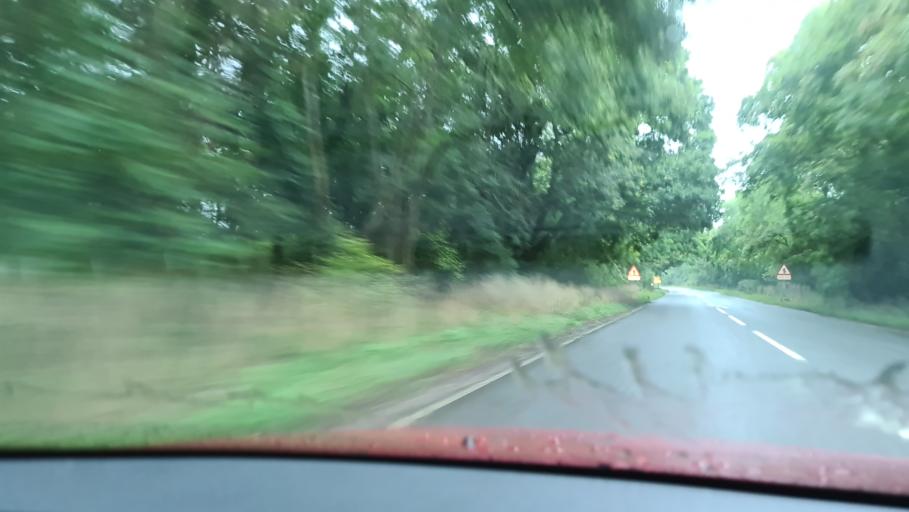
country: GB
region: England
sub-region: Oxfordshire
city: Bicester
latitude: 51.8908
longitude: -1.2264
